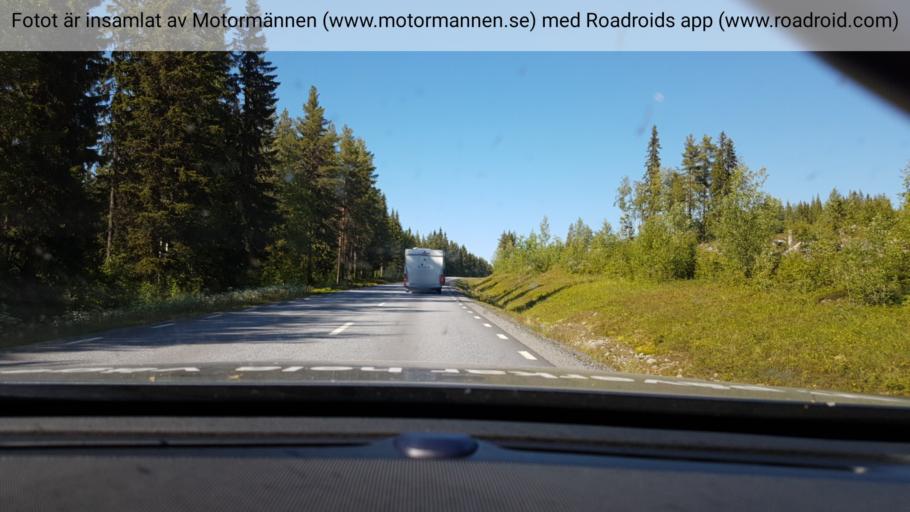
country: SE
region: Vaesterbotten
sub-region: Vilhelmina Kommun
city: Vilhelmina
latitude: 64.5584
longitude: 16.7406
